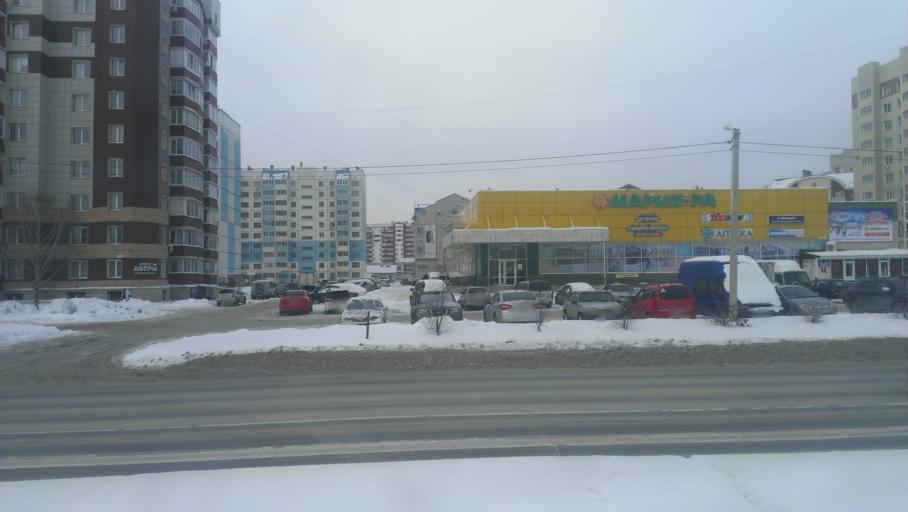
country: RU
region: Altai Krai
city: Novosilikatnyy
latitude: 53.3313
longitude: 83.6929
